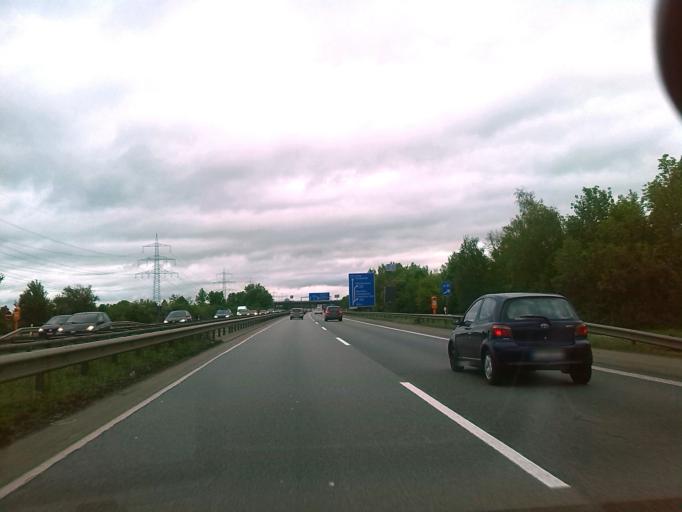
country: DE
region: Rheinland-Pfalz
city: Fussgonheim
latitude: 49.4634
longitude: 8.3139
